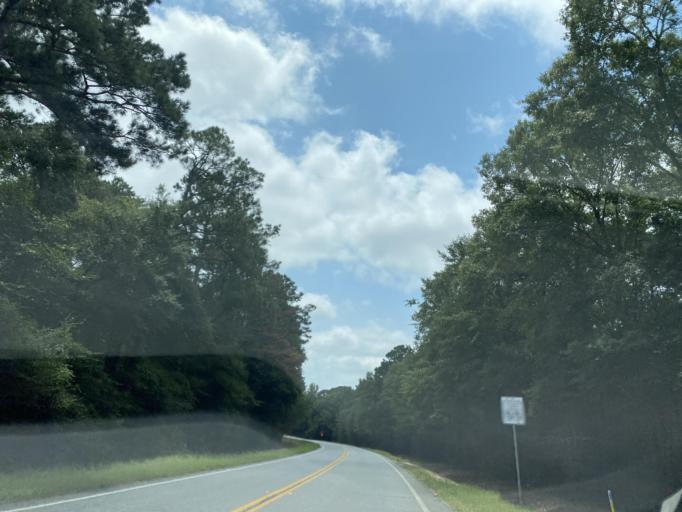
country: US
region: Georgia
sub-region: Wheeler County
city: Alamo
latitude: 32.1400
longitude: -82.7837
